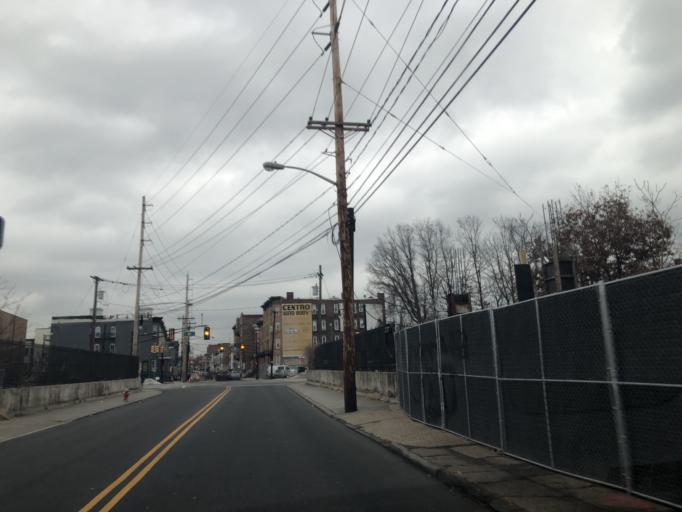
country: US
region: New Jersey
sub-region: Hudson County
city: Jersey City
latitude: 40.7328
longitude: -74.0553
